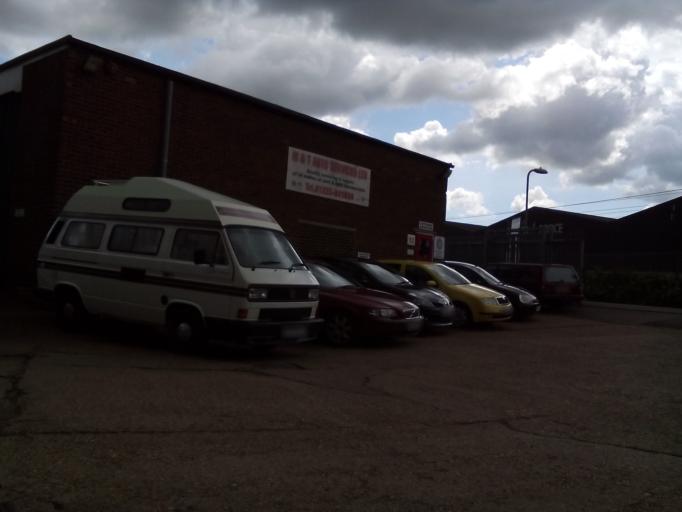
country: GB
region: England
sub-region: Cambridgeshire
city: Cambridge
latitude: 52.2086
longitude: 0.1484
